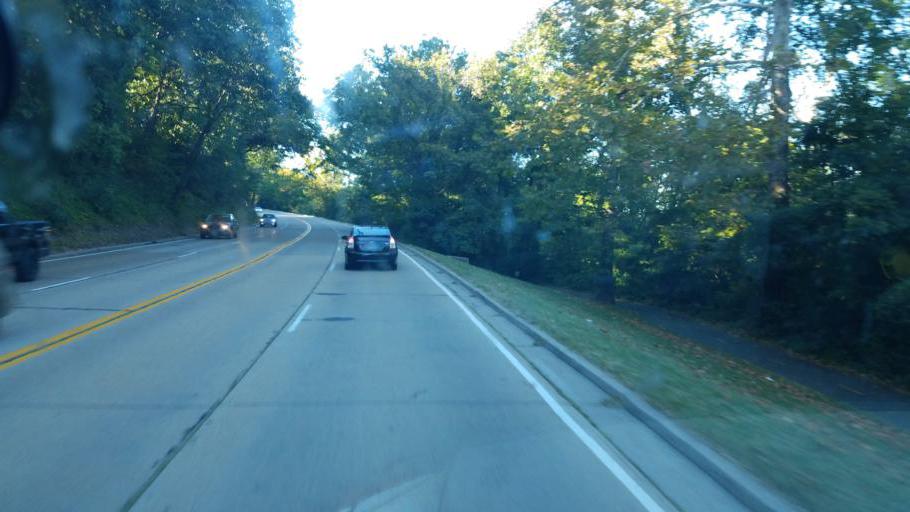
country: US
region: Virginia
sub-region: Fairfax County
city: Fort Hunt
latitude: 38.7574
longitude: -77.0489
